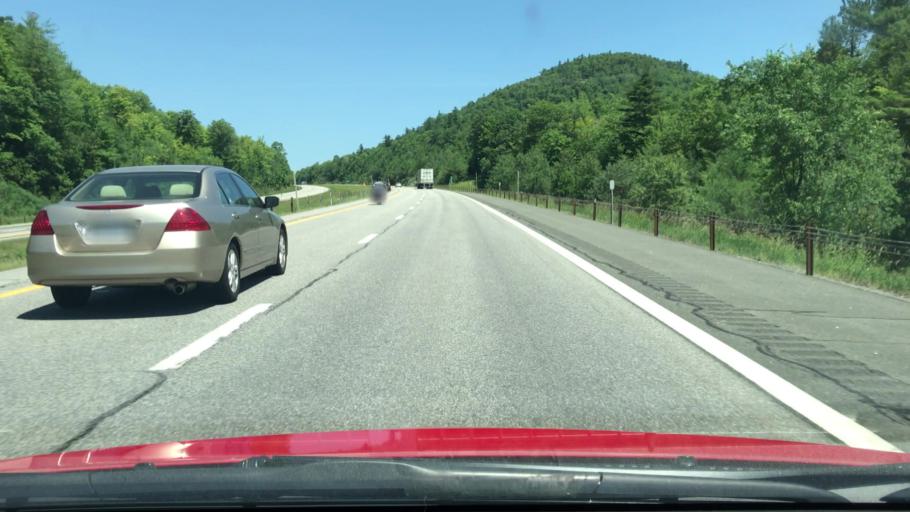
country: US
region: New York
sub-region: Essex County
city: Keeseville
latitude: 44.3892
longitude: -73.5043
